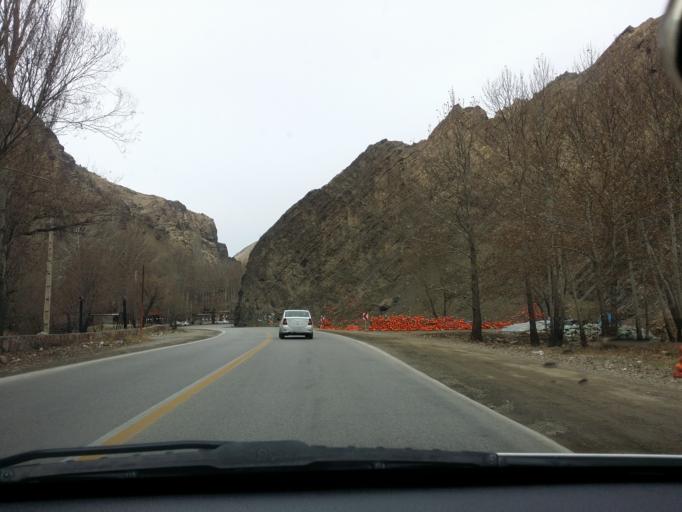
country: IR
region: Tehran
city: Tajrish
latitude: 36.0187
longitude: 51.2695
